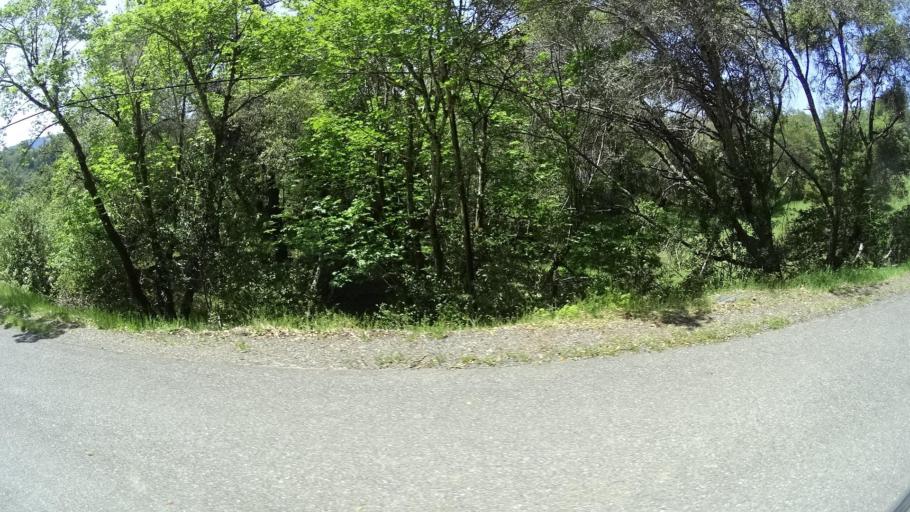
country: US
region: California
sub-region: Humboldt County
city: Redway
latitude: 40.2338
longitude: -123.6181
